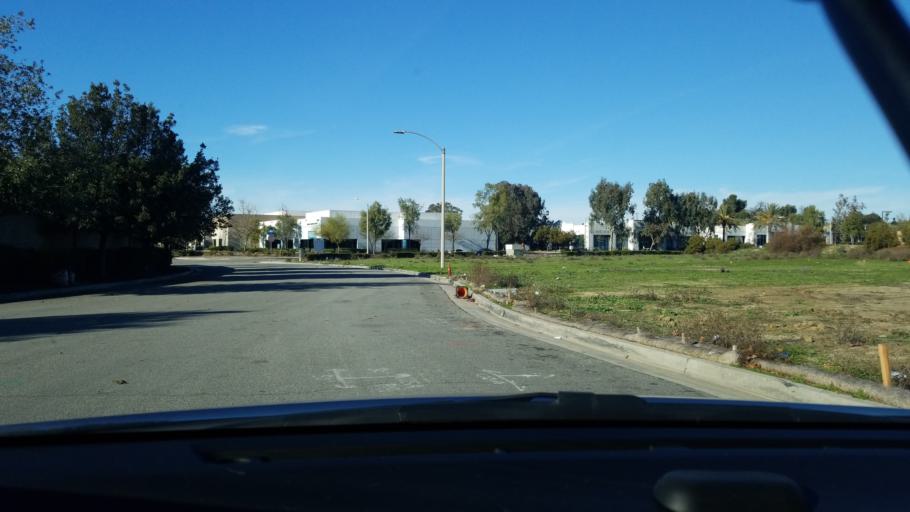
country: US
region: California
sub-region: Riverside County
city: Murrieta Hot Springs
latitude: 33.5316
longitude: -117.1799
